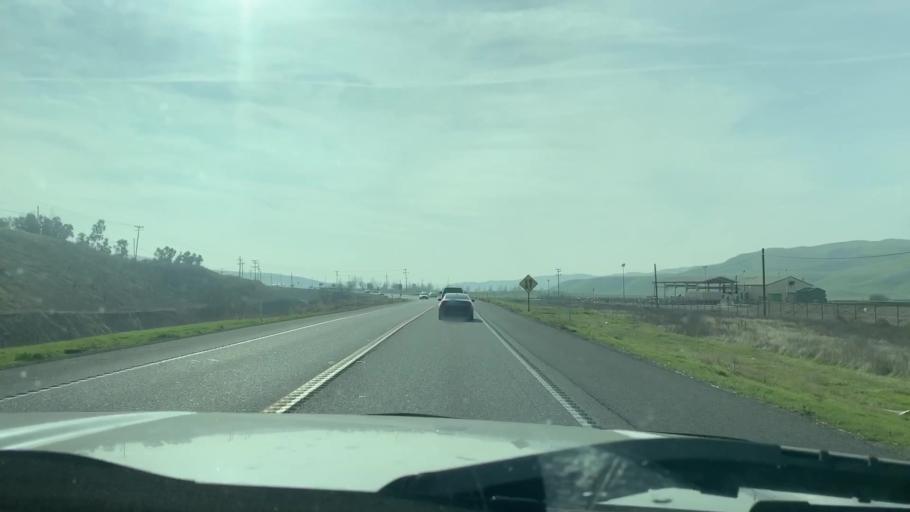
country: US
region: California
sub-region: San Luis Obispo County
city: Shandon
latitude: 35.6904
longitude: -120.3340
